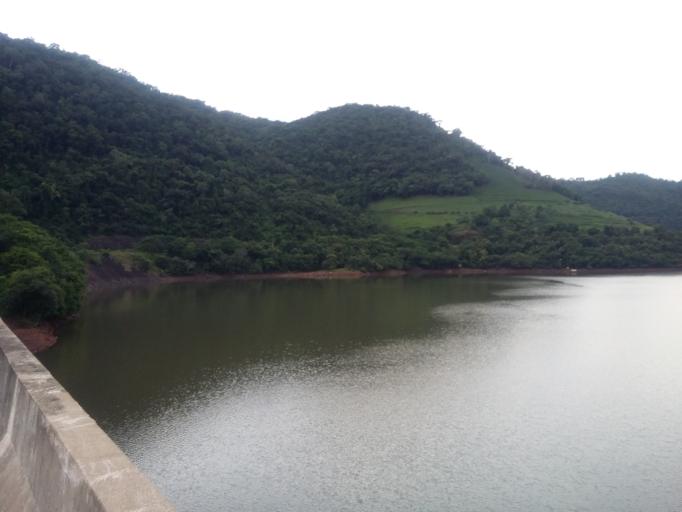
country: BR
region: Santa Catarina
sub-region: Celso Ramos
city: Celso Ramos
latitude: -27.6044
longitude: -51.4696
